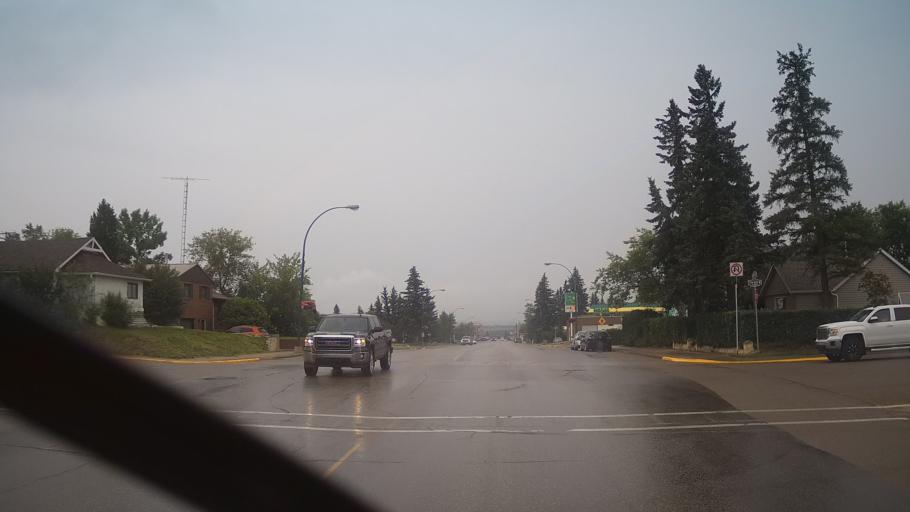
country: CA
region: Saskatchewan
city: Biggar
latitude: 52.0598
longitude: -107.9825
